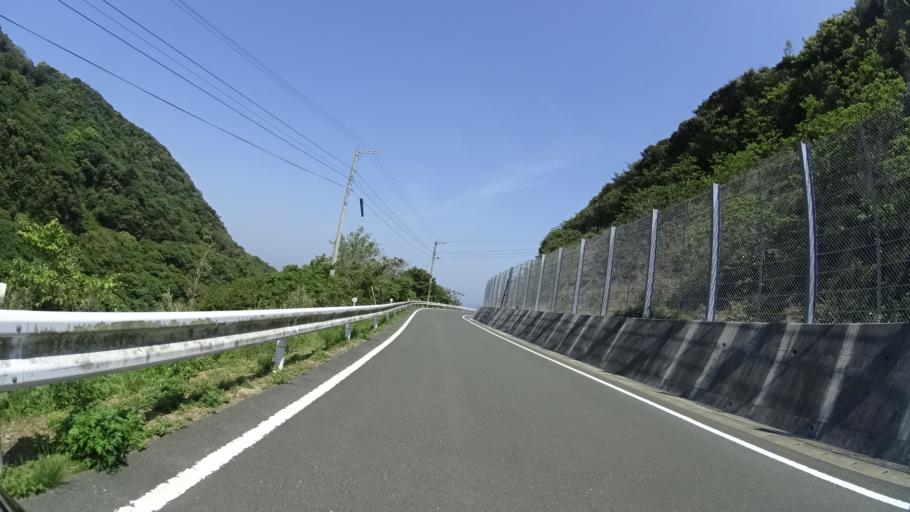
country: JP
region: Oita
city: Tsukumiura
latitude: 33.3564
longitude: 132.0383
